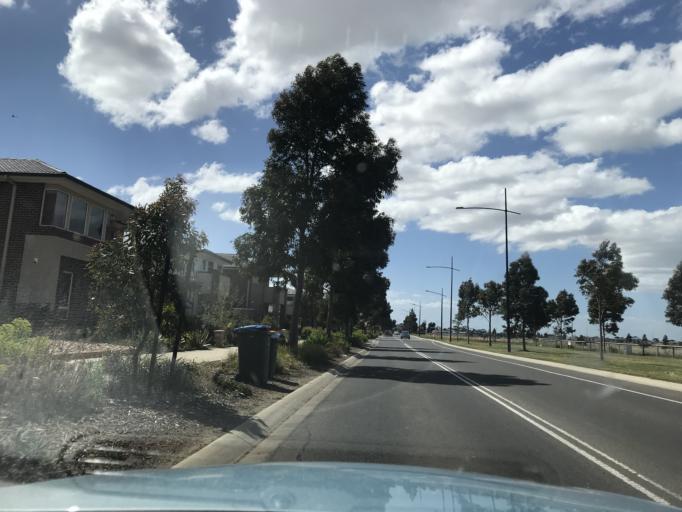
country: AU
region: Victoria
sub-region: Wyndham
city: Williams Landing
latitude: -37.8637
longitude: 144.7429
